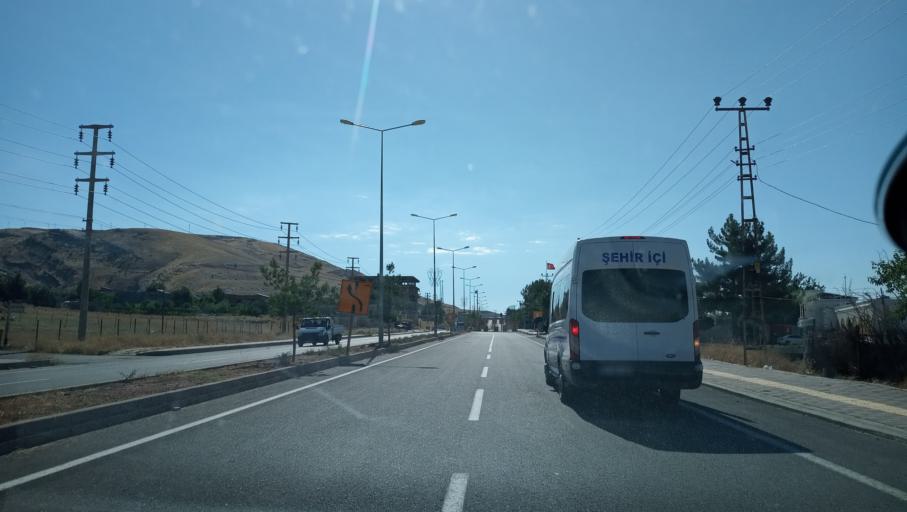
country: TR
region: Diyarbakir
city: Silvan
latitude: 38.1355
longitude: 41.0285
